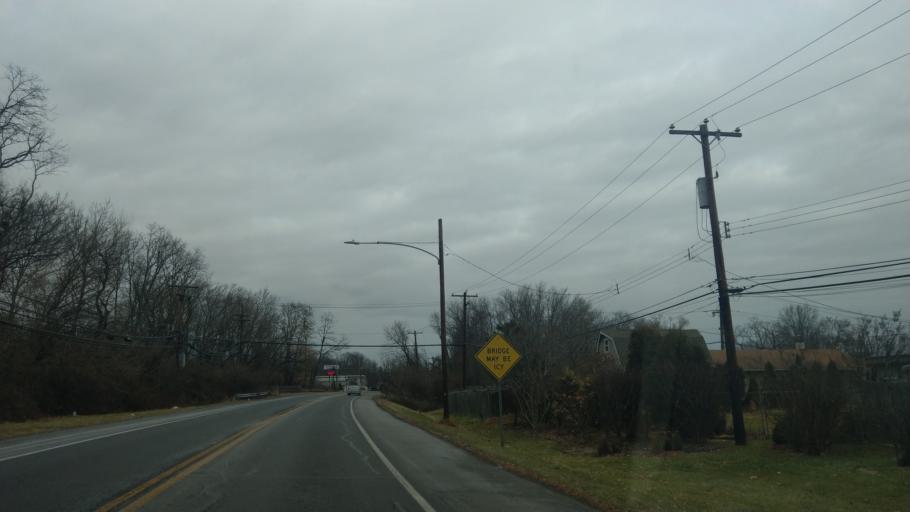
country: US
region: Pennsylvania
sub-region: Bucks County
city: Hulmeville
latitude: 40.1378
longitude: -74.8744
